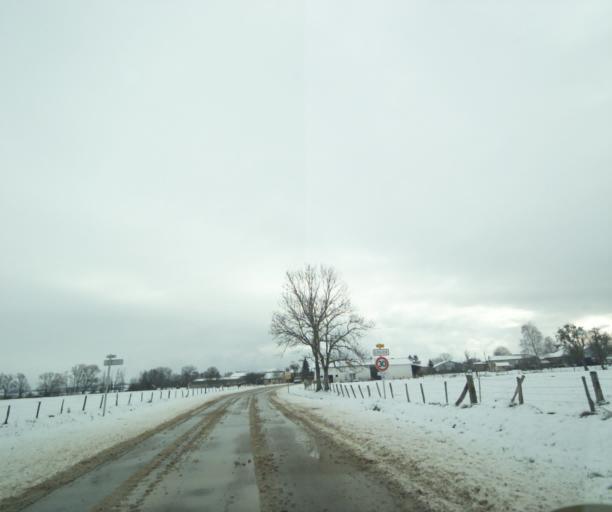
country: FR
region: Champagne-Ardenne
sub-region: Departement de la Haute-Marne
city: Montier-en-Der
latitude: 48.4398
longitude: 4.7105
